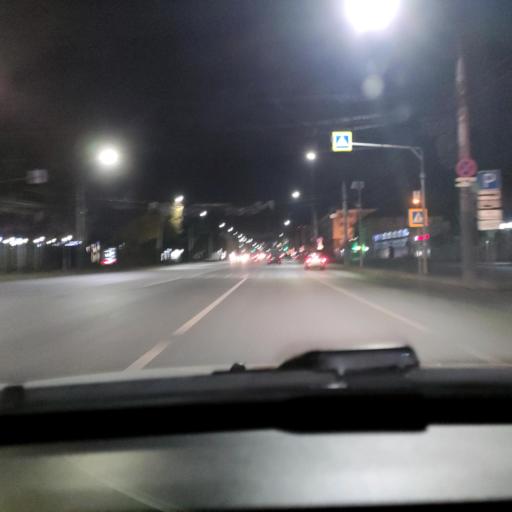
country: RU
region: Voronezj
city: Voronezh
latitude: 51.6654
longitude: 39.1897
